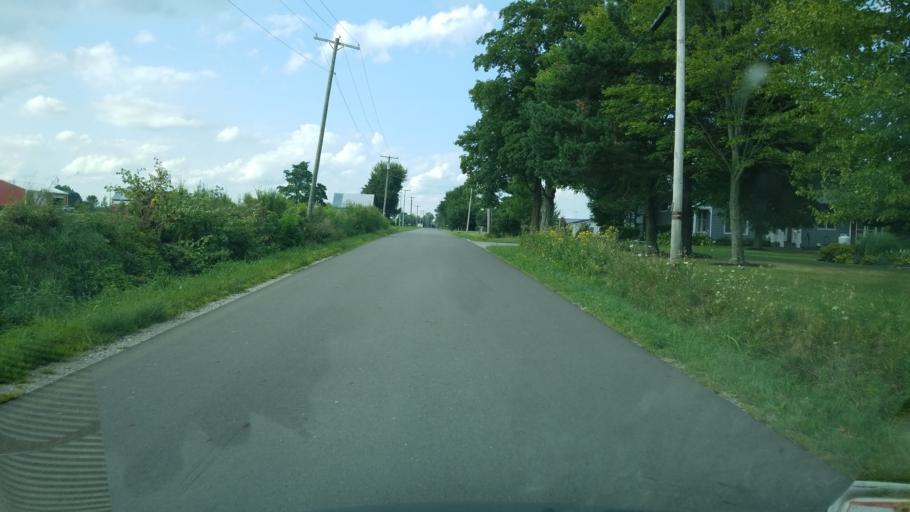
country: US
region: Ohio
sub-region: Morrow County
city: Cardington
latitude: 40.4686
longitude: -82.8958
